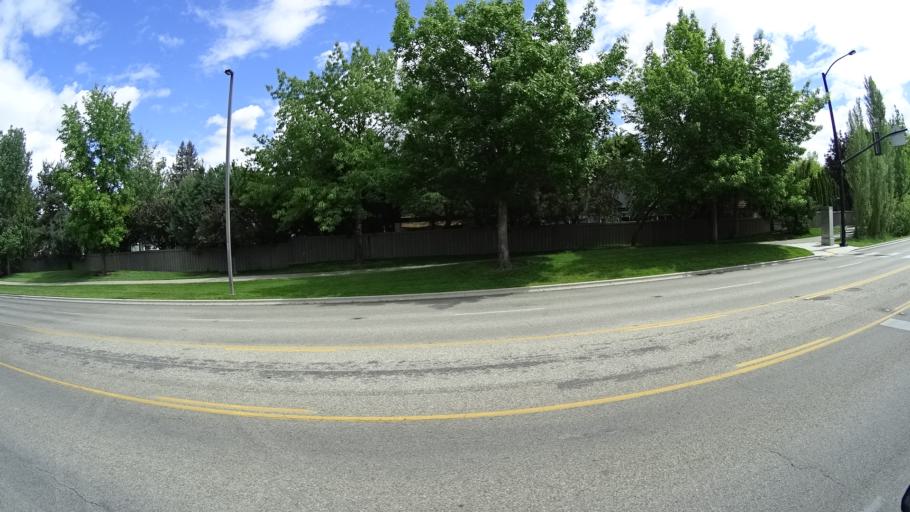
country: US
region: Idaho
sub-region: Ada County
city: Boise
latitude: 43.5759
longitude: -116.1564
